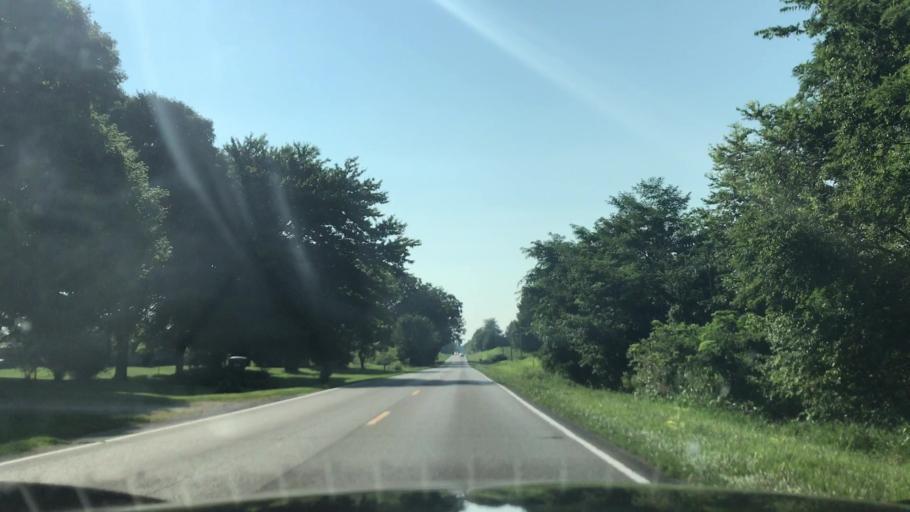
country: US
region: Kentucky
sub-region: Hart County
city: Horse Cave
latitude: 37.1738
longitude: -85.8627
